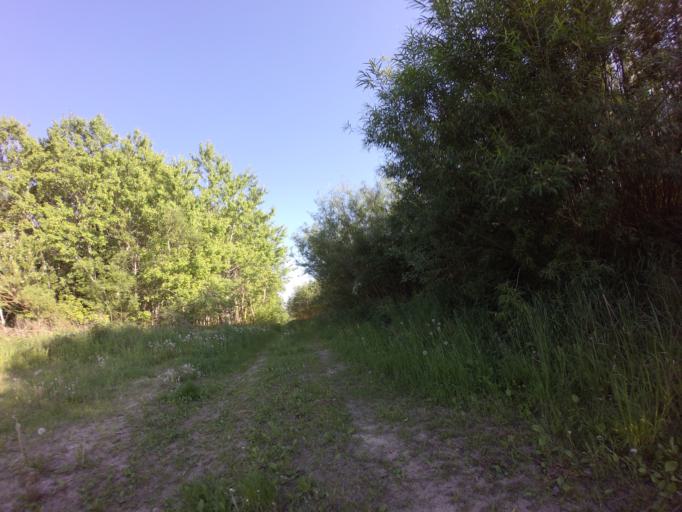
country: PL
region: West Pomeranian Voivodeship
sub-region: Powiat choszczenski
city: Choszczno
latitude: 53.1323
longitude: 15.4347
